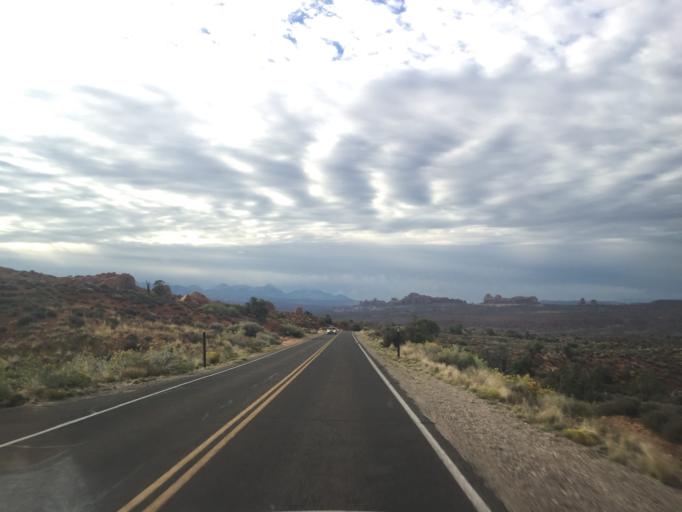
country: US
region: Utah
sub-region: Grand County
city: Moab
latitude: 38.7550
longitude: -109.5741
